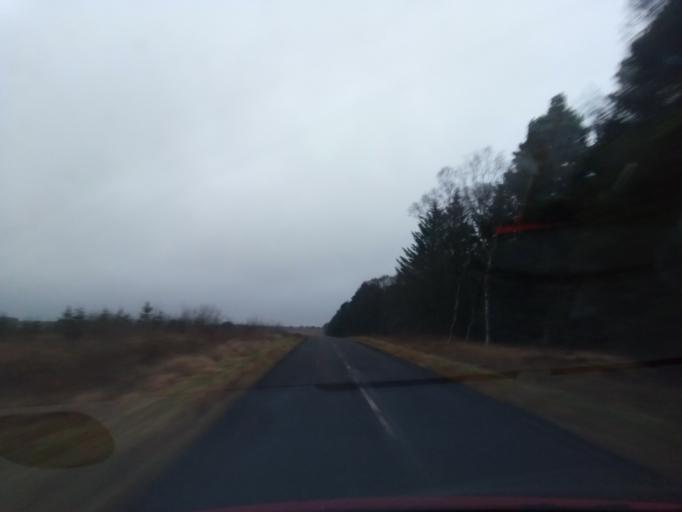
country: GB
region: England
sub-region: Northumberland
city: Rothley
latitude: 55.2040
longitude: -2.0088
